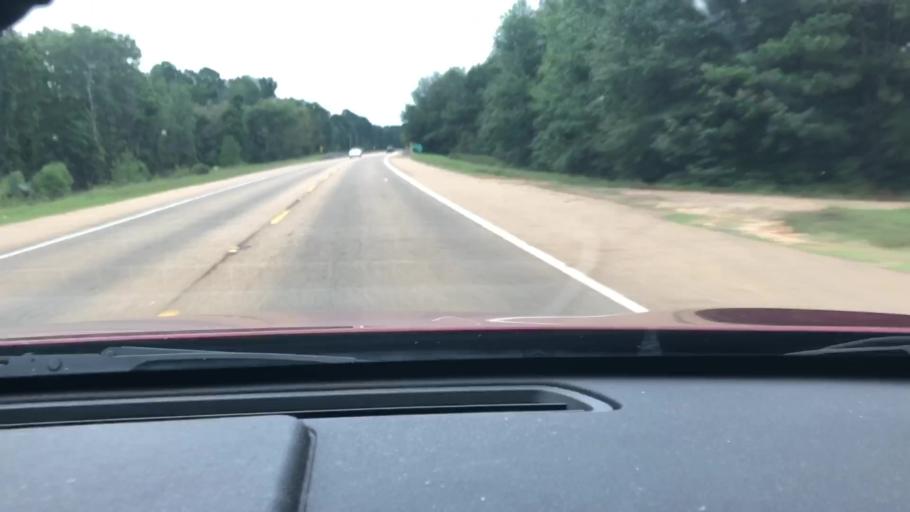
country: US
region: Arkansas
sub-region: Lafayette County
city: Stamps
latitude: 33.3589
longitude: -93.4162
